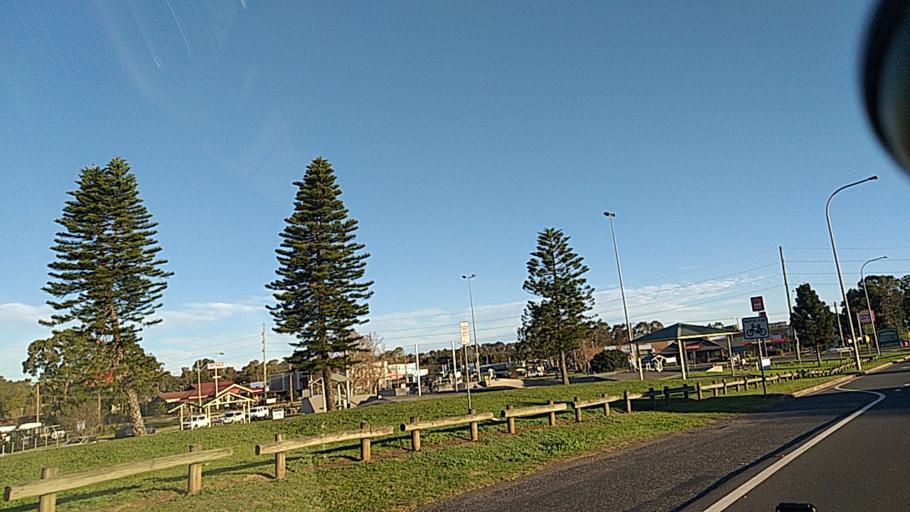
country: AU
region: New South Wales
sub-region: Campbelltown Municipality
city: Leumeah
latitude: -34.0486
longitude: 150.8280
